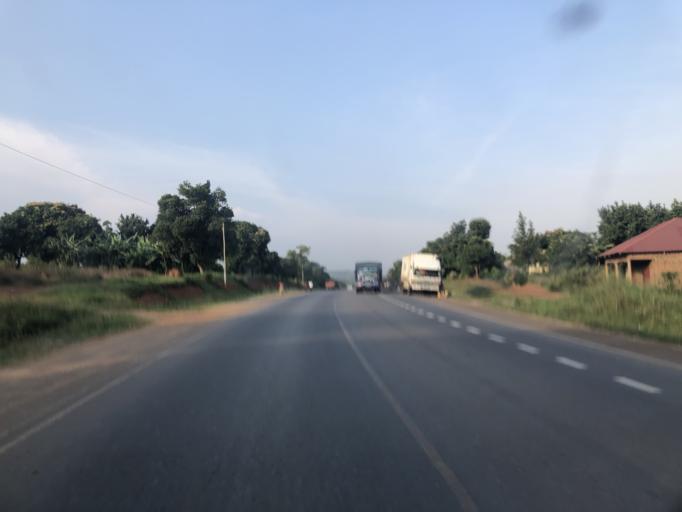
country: UG
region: Central Region
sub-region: Mpigi District
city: Mpigi
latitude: 0.1610
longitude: 32.2317
